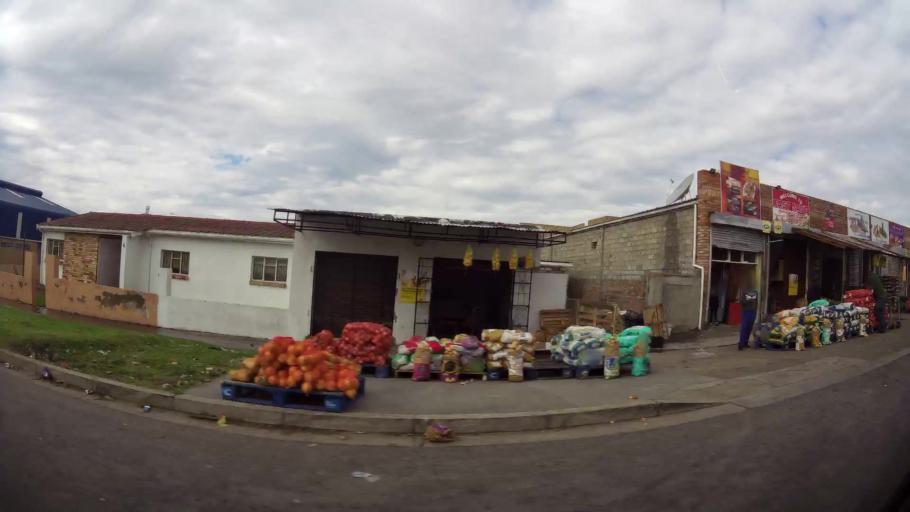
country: ZA
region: Eastern Cape
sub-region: Nelson Mandela Bay Metropolitan Municipality
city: Port Elizabeth
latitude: -33.9313
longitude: 25.5769
